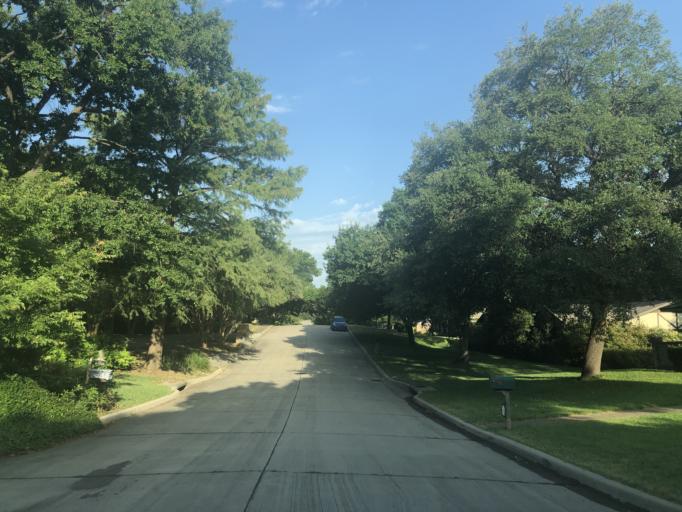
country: US
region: Texas
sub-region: Dallas County
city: Grand Prairie
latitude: 32.7615
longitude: -97.0245
